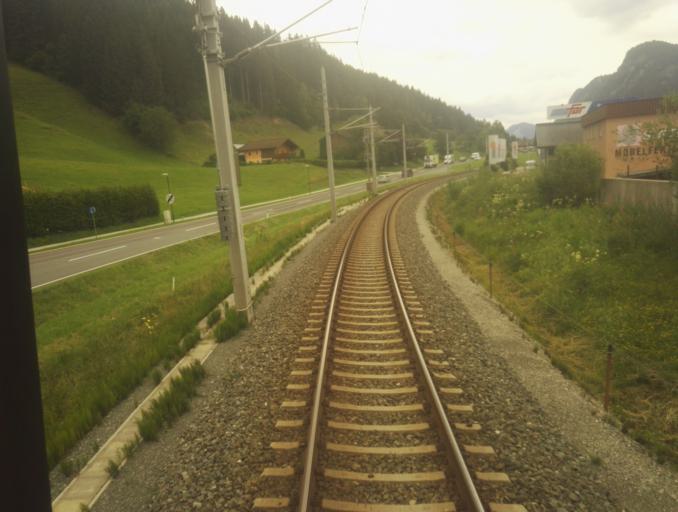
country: AT
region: Salzburg
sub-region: Politischer Bezirk Sankt Johann im Pongau
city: Radstadt
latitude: 47.3860
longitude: 13.4738
